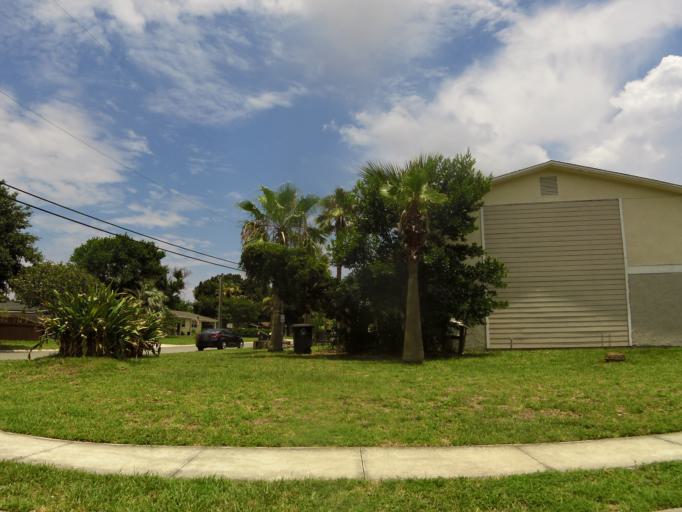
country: US
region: Florida
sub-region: Duval County
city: Atlantic Beach
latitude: 30.3267
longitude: -81.4103
